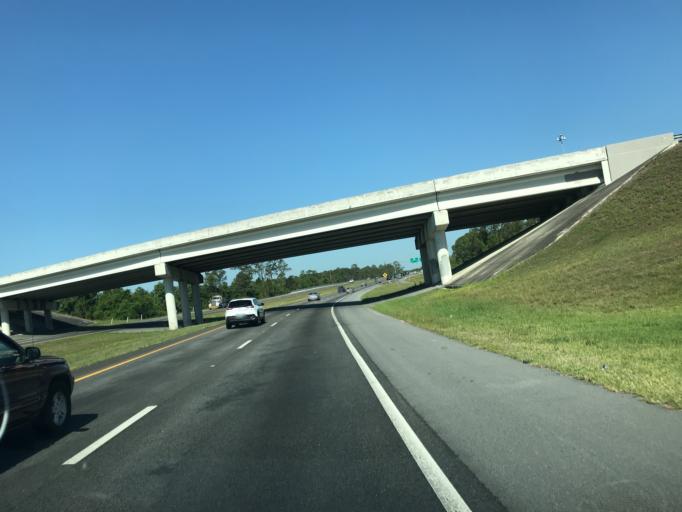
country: US
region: Florida
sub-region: Osceola County
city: Celebration
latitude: 28.3587
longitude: -81.5157
